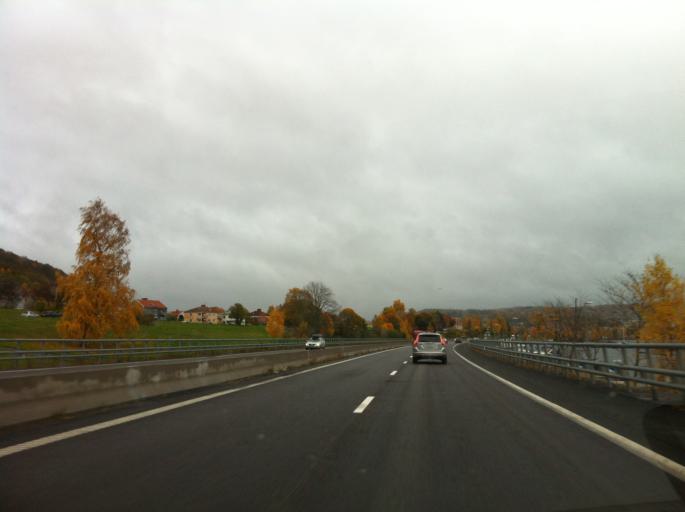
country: SE
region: Joenkoeping
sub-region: Jonkopings Kommun
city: Huskvarna
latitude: 57.8059
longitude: 14.2719
